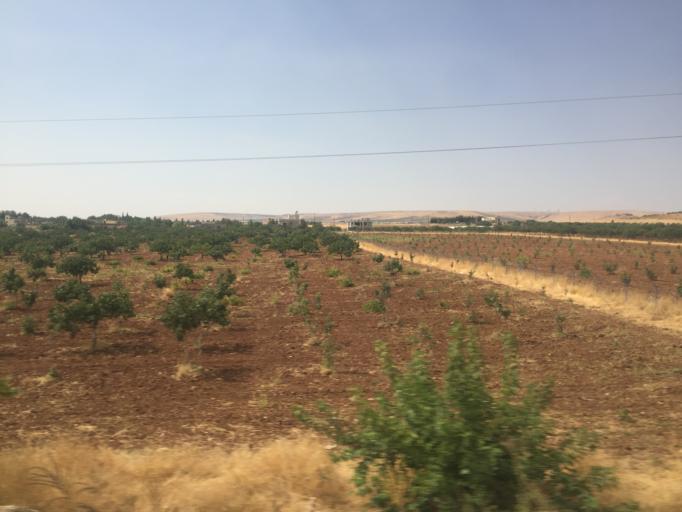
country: TR
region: Sanliurfa
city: Akziyaret
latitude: 37.3875
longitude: 38.8567
